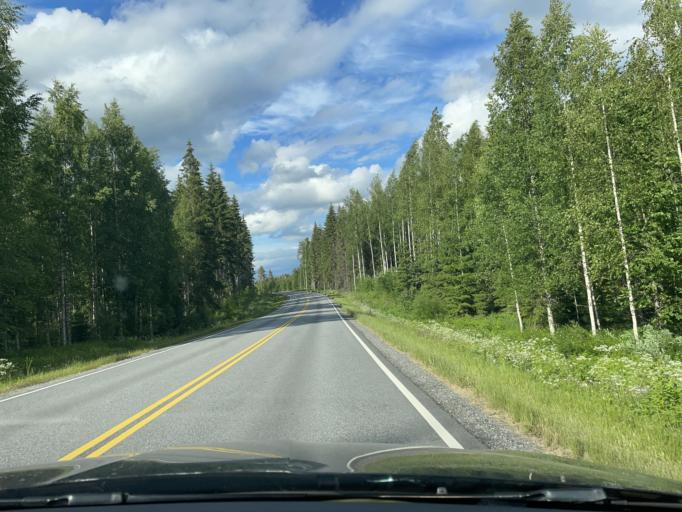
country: FI
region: Central Finland
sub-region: Jaemsae
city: Jaemsaenkoski
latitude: 62.0366
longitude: 25.1395
